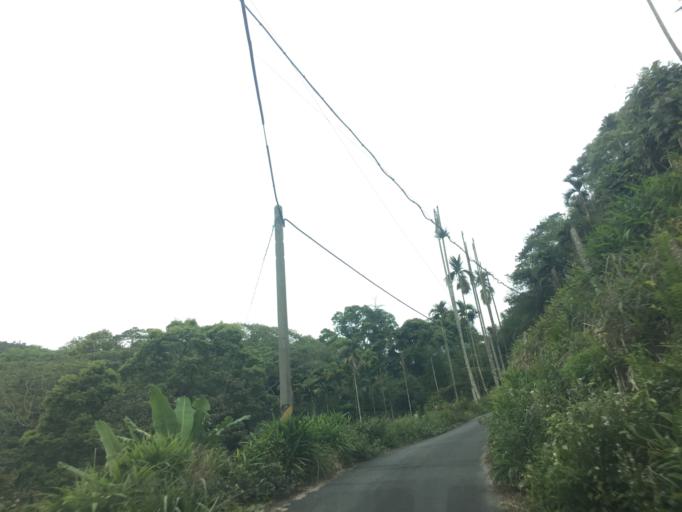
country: TW
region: Taiwan
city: Zhongxing New Village
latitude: 23.9702
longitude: 120.8248
